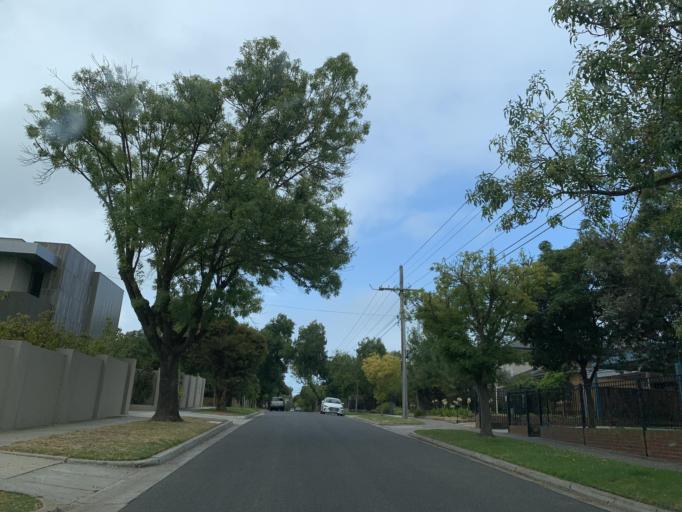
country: AU
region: Victoria
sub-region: Bayside
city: Hampton East
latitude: -37.9252
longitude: 145.0198
